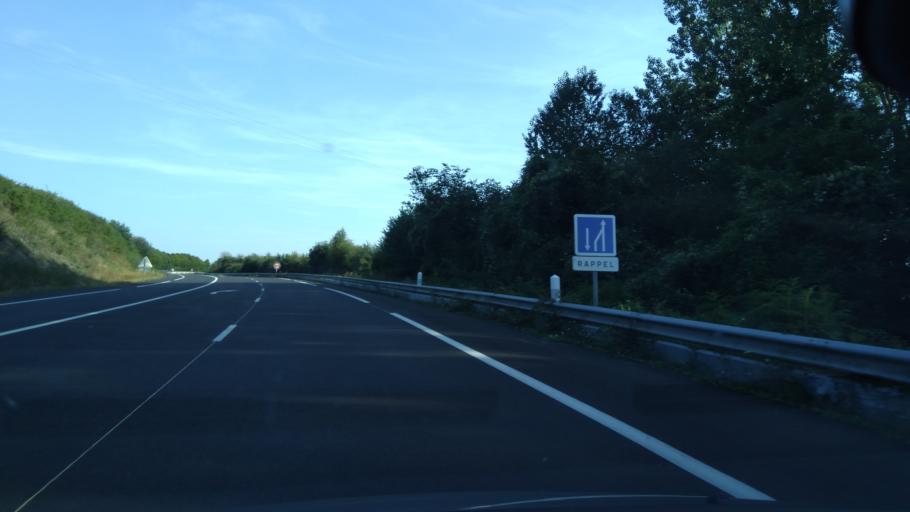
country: FR
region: Pays de la Loire
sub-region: Departement de la Mayenne
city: Entrammes
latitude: 47.9658
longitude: -0.7075
